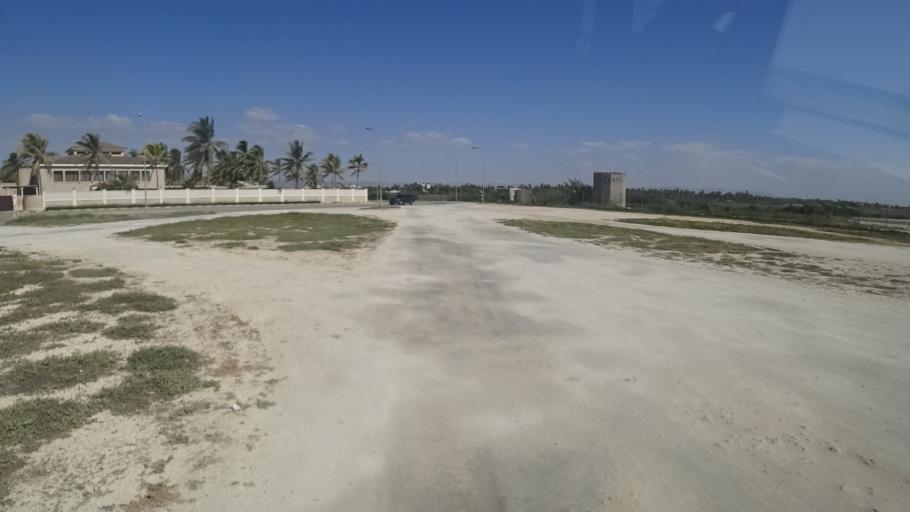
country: OM
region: Zufar
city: Salalah
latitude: 16.9946
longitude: 54.0651
